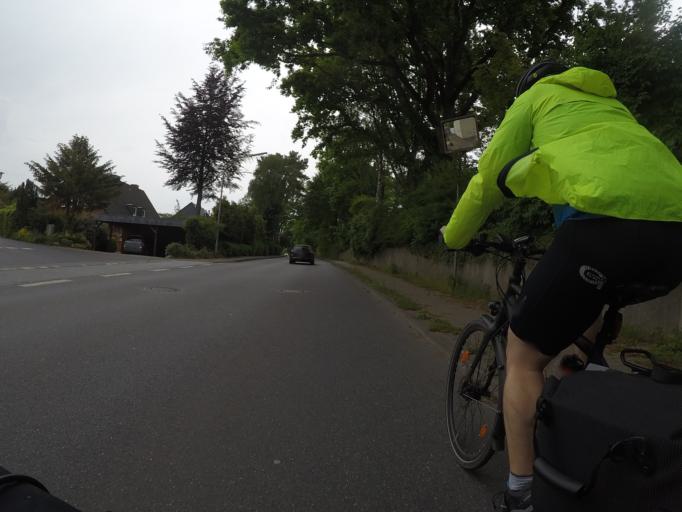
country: DE
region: Schleswig-Holstein
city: Kisdorf
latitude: 53.7935
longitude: 10.0062
